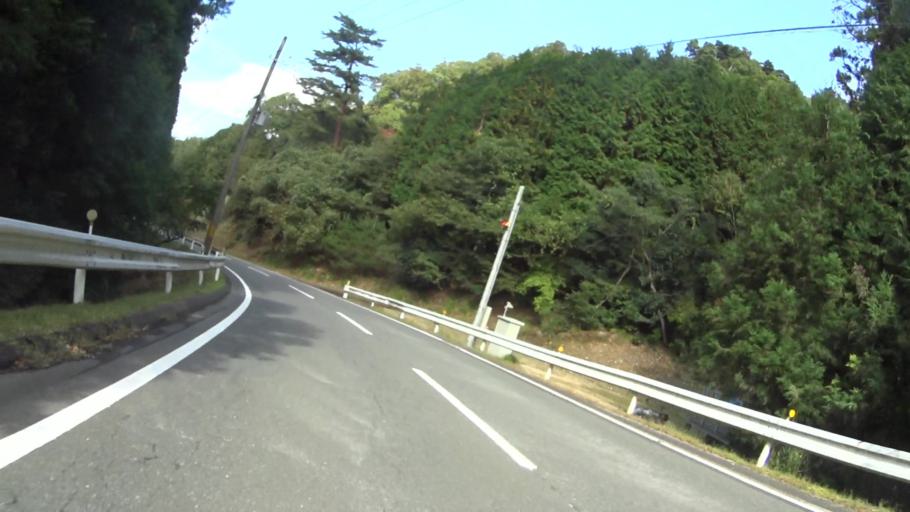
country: JP
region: Hyogo
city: Toyooka
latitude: 35.5356
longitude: 134.9791
